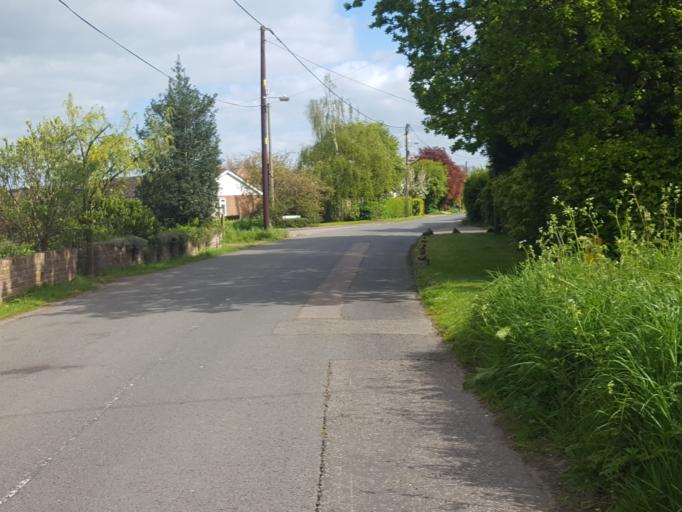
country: GB
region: England
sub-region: Essex
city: Frinton-on-Sea
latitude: 51.8340
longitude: 1.2072
